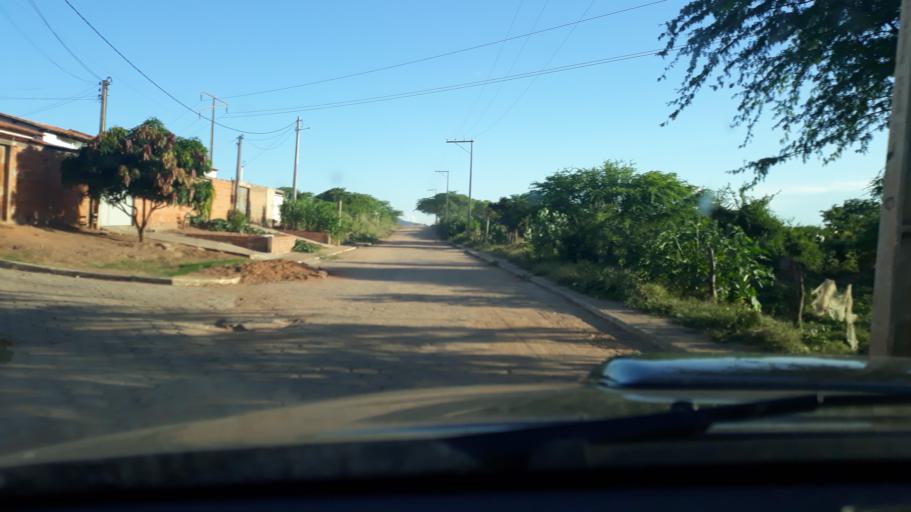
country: BR
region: Bahia
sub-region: Riacho De Santana
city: Riacho de Santana
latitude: -13.7843
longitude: -42.7137
